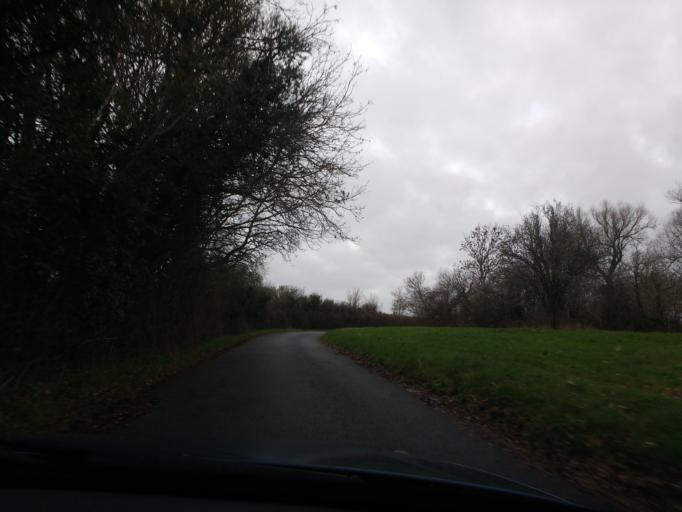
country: GB
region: England
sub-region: Isle of Wight
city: Shalfleet
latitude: 50.7121
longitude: -1.4017
